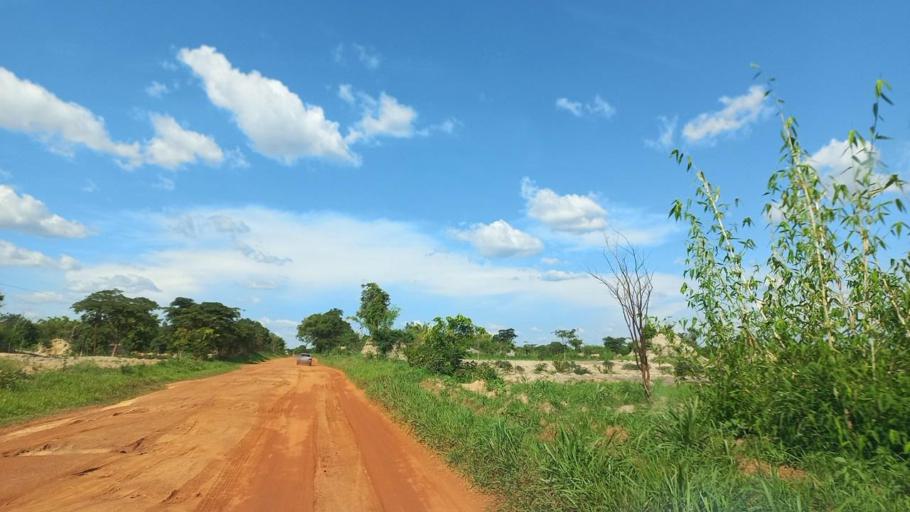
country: ZM
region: Copperbelt
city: Kitwe
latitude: -12.8626
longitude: 28.3816
